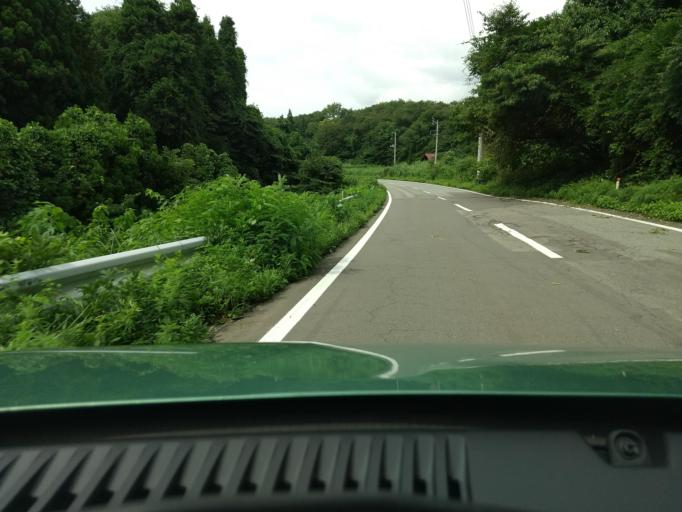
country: JP
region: Akita
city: Akita
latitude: 39.7262
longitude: 140.1832
